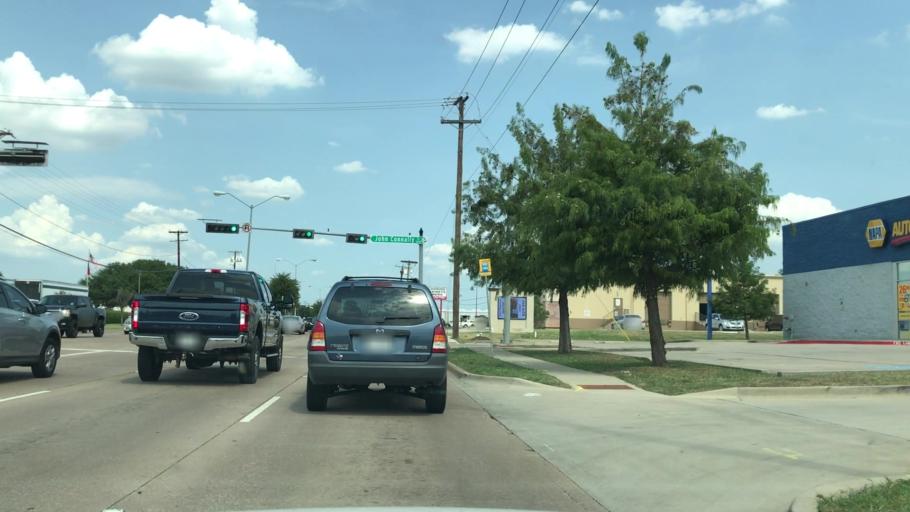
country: US
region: Texas
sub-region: Dallas County
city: Carrollton
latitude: 32.9532
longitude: -96.8646
